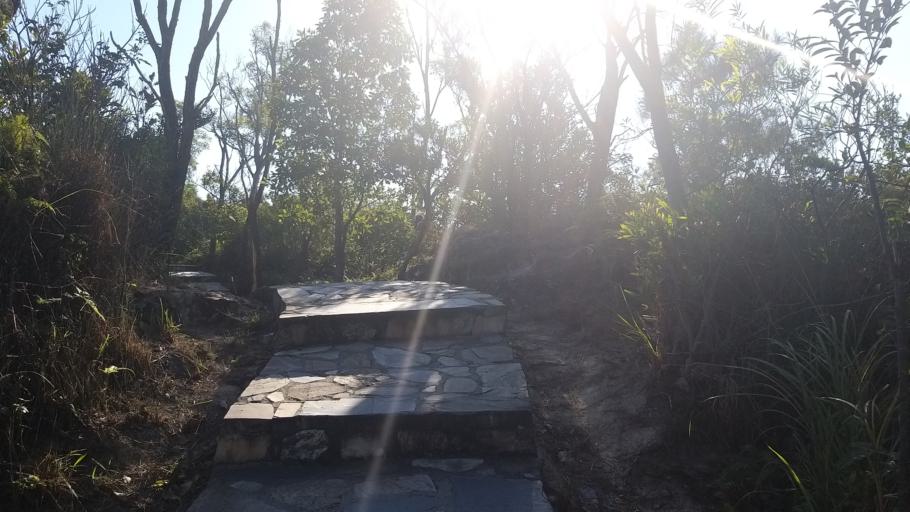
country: HK
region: Tuen Mun
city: Tuen Mun
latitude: 22.4013
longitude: 113.9878
